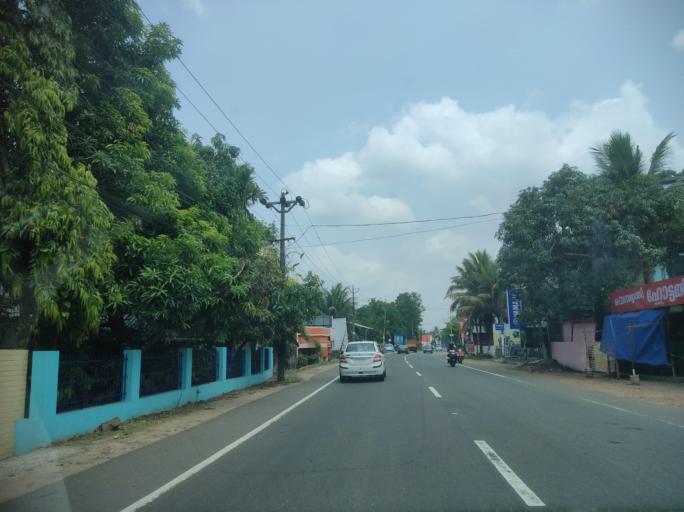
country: IN
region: Kerala
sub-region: Kottayam
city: Changanacheri
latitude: 9.4179
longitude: 76.5488
